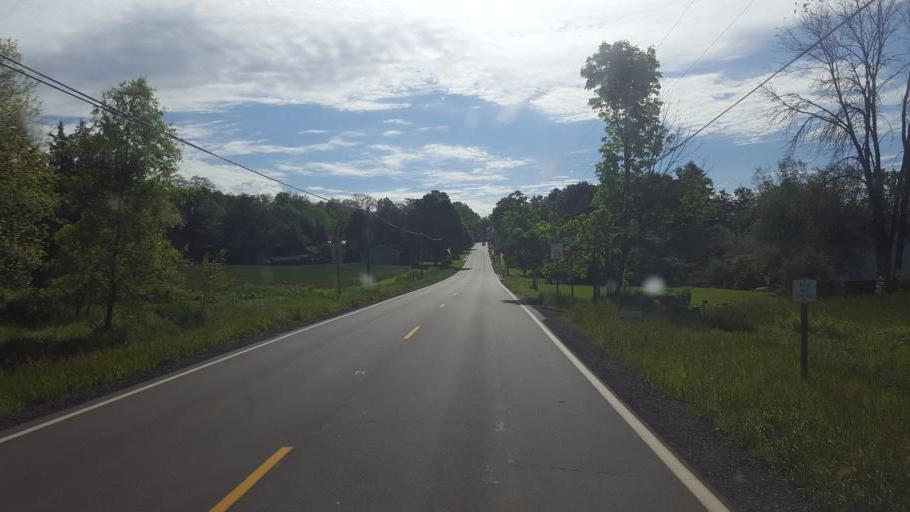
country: US
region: Ohio
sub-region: Medina County
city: Wadsworth
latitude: 41.0992
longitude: -81.7415
